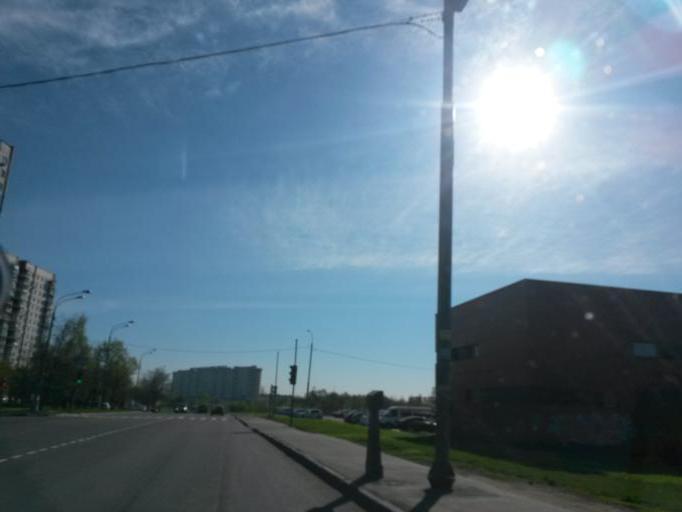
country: RU
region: Moscow
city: Zyablikovo
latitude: 55.6145
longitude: 37.7528
